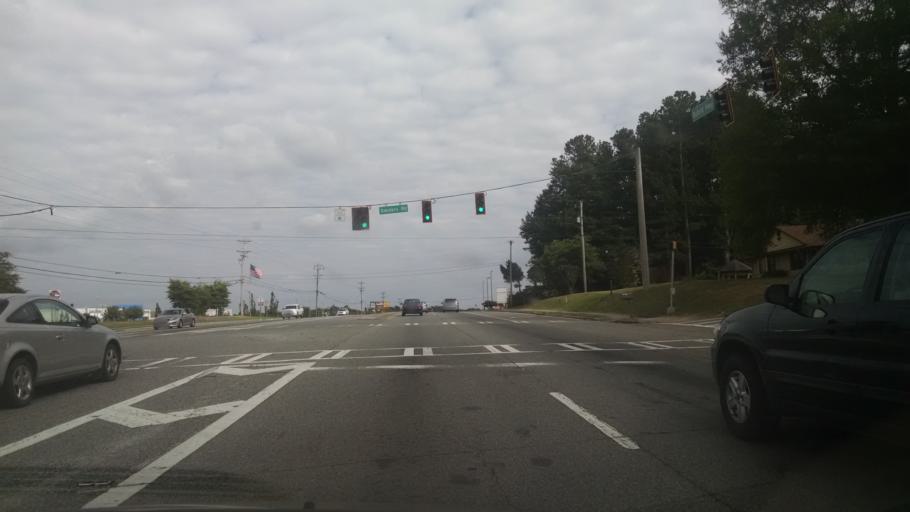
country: US
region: Georgia
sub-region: Forsyth County
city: Cumming
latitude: 34.1772
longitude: -84.1306
